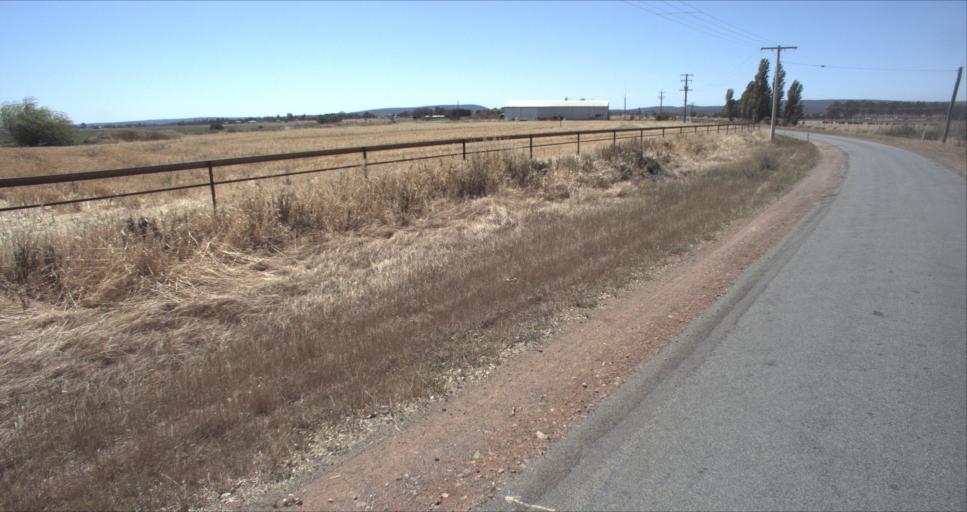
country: AU
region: New South Wales
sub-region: Leeton
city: Leeton
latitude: -34.5396
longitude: 146.4410
